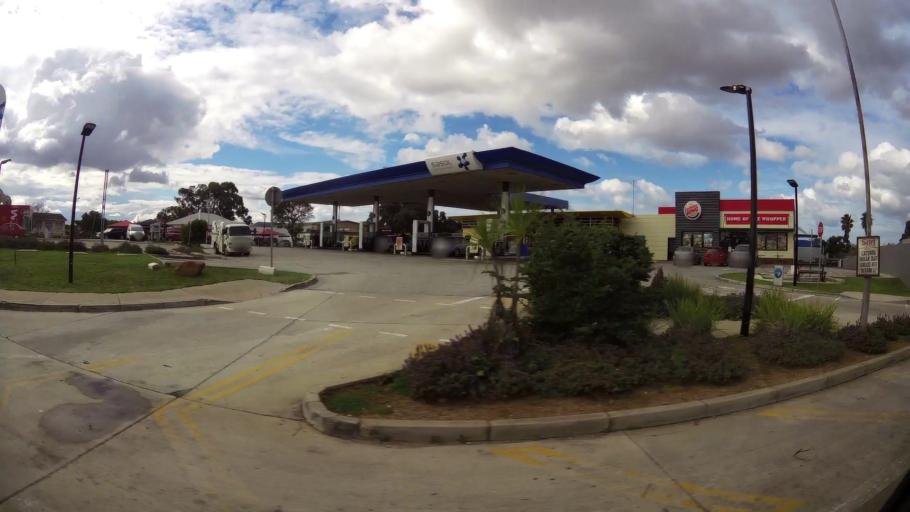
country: ZA
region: Eastern Cape
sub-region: Nelson Mandela Bay Metropolitan Municipality
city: Port Elizabeth
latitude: -33.9438
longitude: 25.5529
